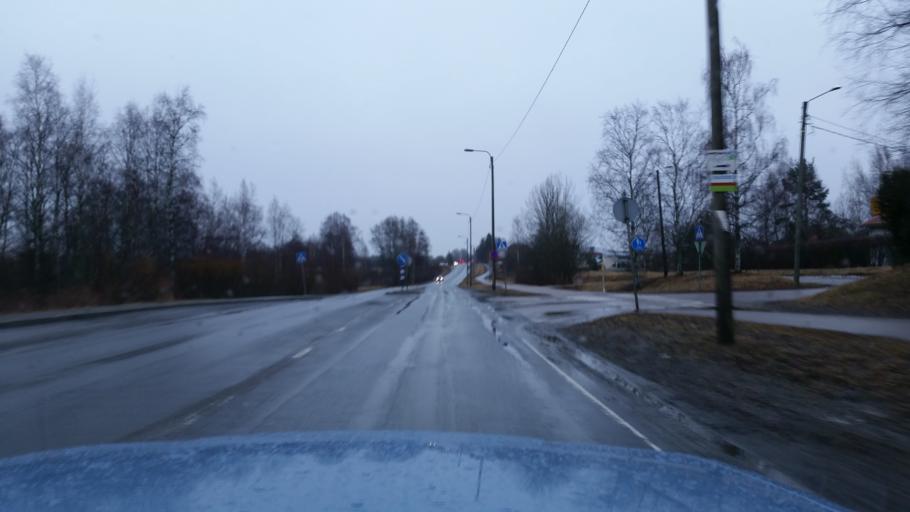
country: FI
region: Pirkanmaa
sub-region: Tampere
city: Tampere
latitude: 61.4801
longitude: 23.8155
